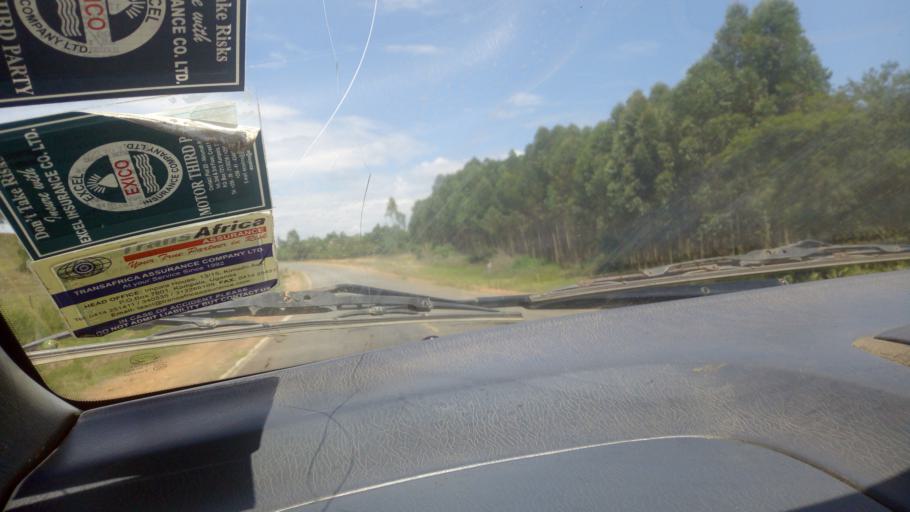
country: UG
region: Western Region
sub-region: Buhweju District
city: Buhweju
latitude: -0.2691
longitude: 30.5621
